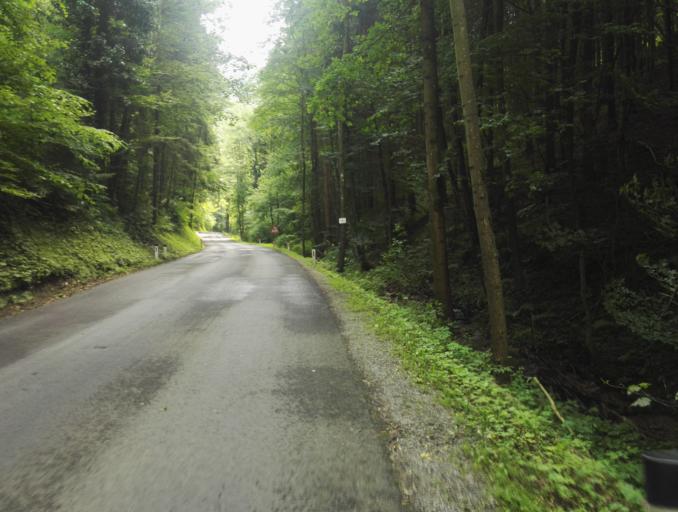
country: AT
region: Styria
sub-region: Politischer Bezirk Graz-Umgebung
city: Gratwein
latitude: 47.0953
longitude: 15.3155
